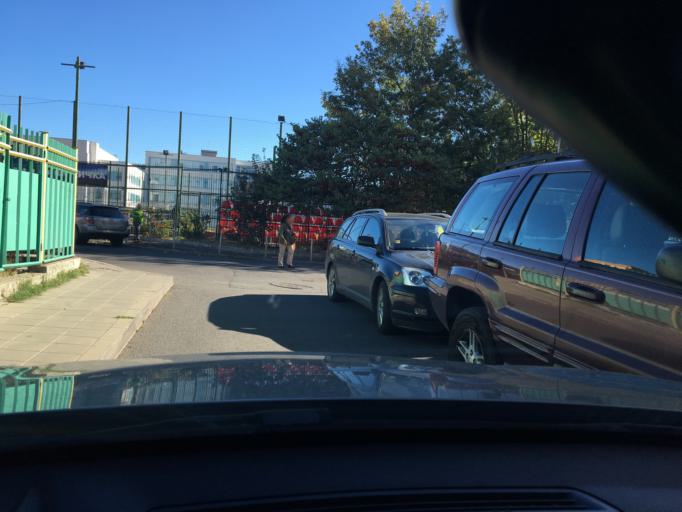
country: BG
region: Burgas
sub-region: Obshtina Burgas
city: Burgas
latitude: 42.5215
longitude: 27.4501
